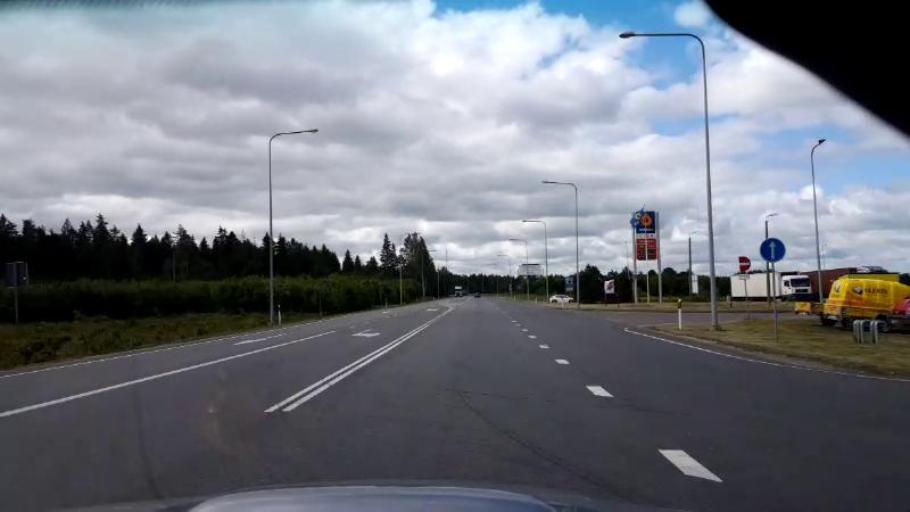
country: EE
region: Raplamaa
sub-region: Maerjamaa vald
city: Marjamaa
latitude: 58.9201
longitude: 24.4577
